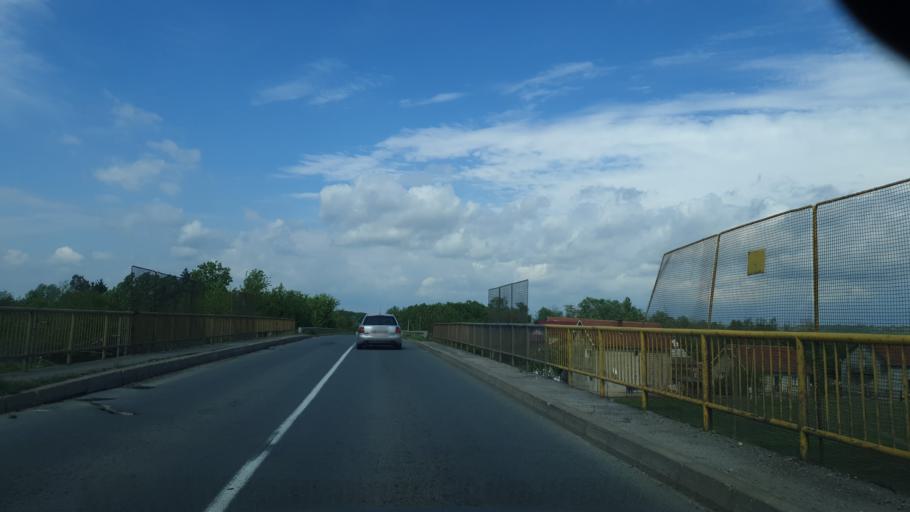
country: RS
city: Zvecka
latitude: 44.6084
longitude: 20.1552
